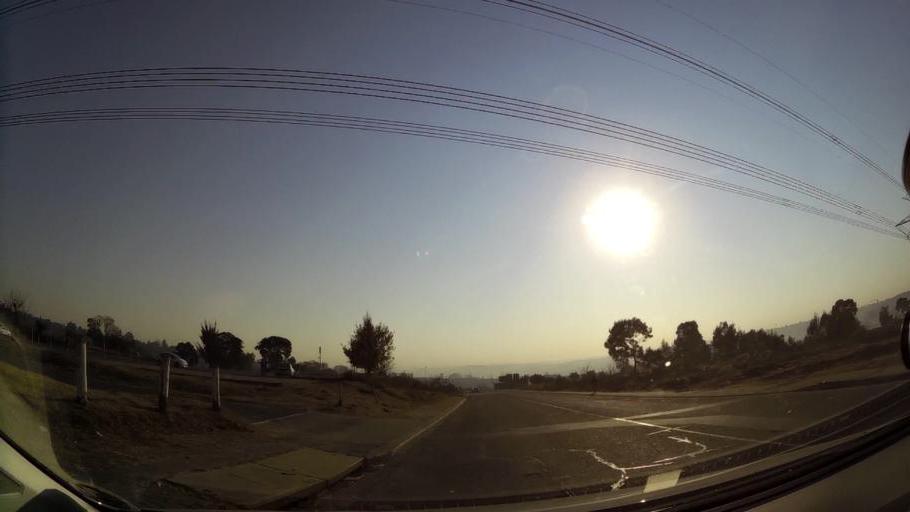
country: ZA
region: Gauteng
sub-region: City of Johannesburg Metropolitan Municipality
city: Modderfontein
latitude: -26.0890
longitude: 28.1028
